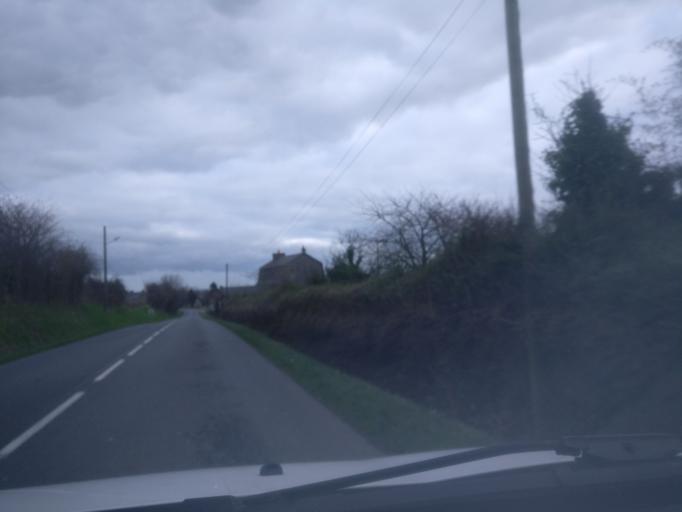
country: FR
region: Lower Normandy
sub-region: Departement de la Manche
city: Marcey-les-Greves
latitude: 48.6847
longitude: -1.3831
